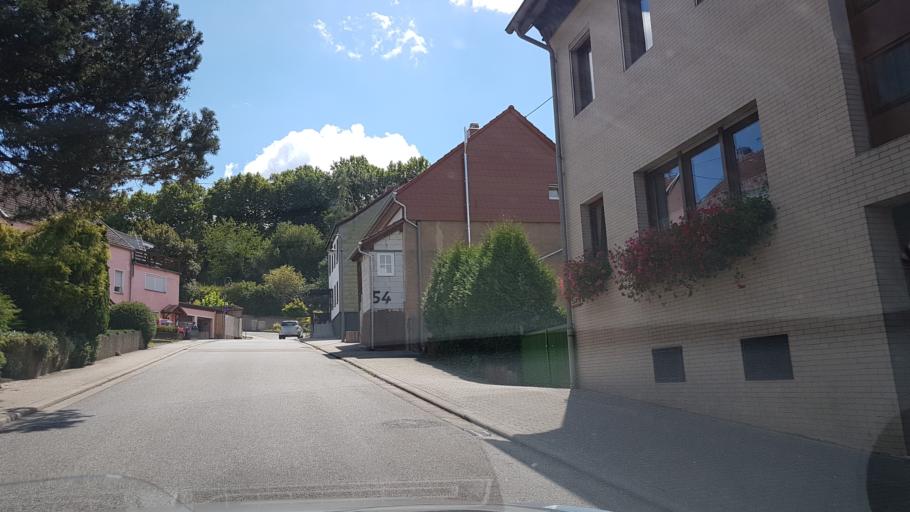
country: DE
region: Saarland
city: Illingen
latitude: 49.3711
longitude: 7.0826
